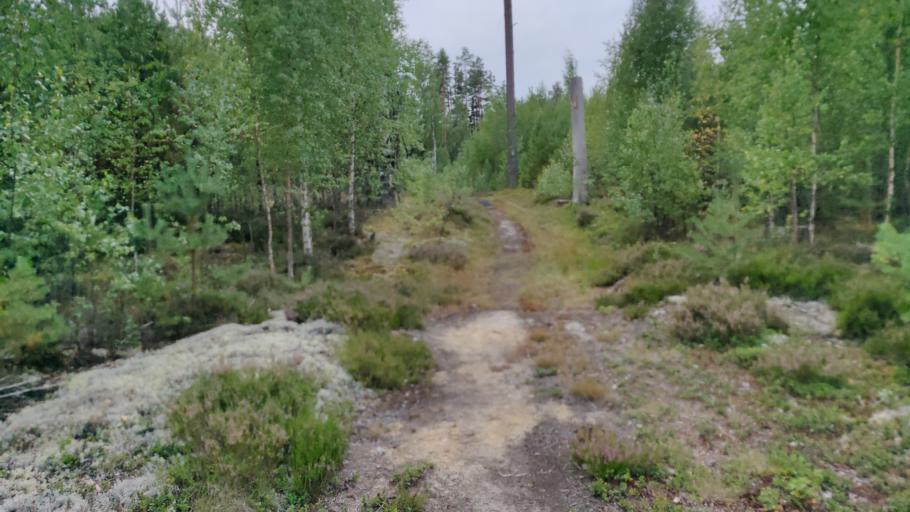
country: SE
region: Vaermland
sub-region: Hagfors Kommun
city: Hagfors
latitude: 60.0191
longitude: 13.5482
